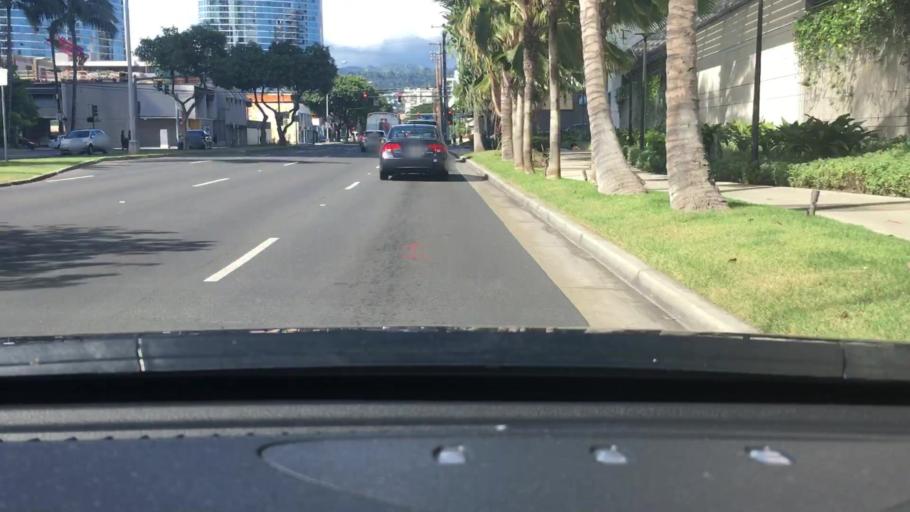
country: US
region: Hawaii
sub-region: Honolulu County
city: Honolulu
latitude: 21.2924
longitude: -157.8471
